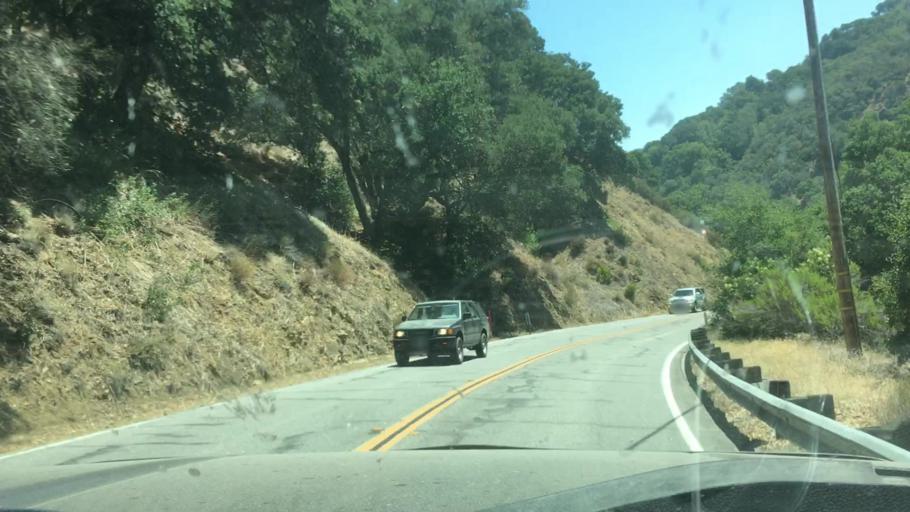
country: US
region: California
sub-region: San Luis Obispo County
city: Atascadero
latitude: 35.4507
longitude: -120.6987
